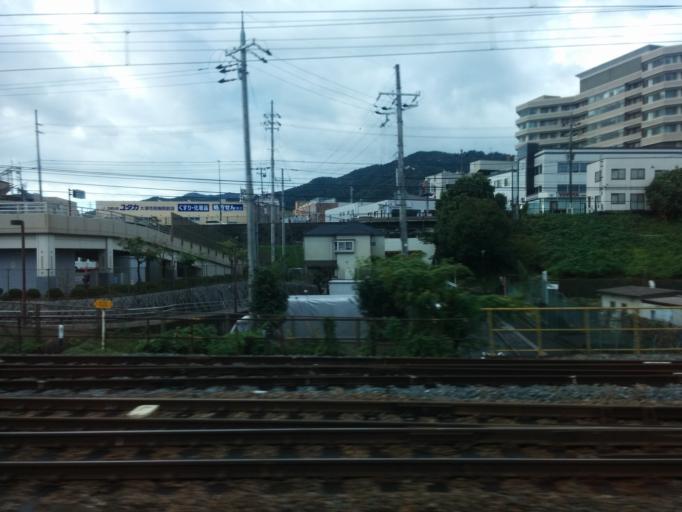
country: JP
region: Shiga Prefecture
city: Otsu-shi
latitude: 35.0011
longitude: 135.8780
